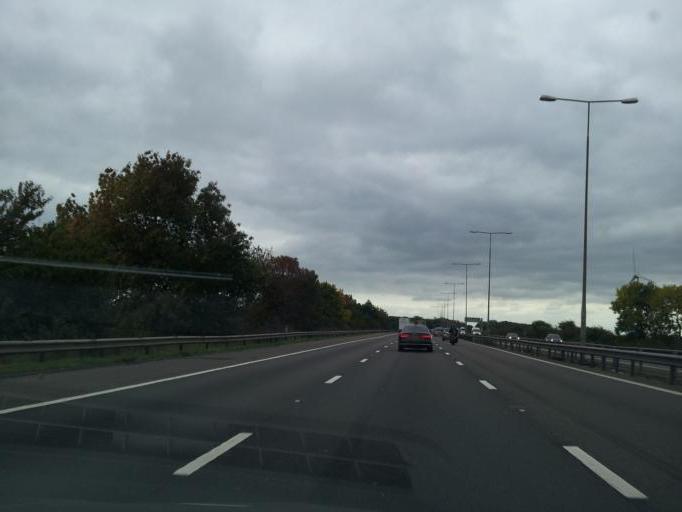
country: GB
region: England
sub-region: Northamptonshire
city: Hartwell
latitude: 52.1664
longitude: -0.8613
